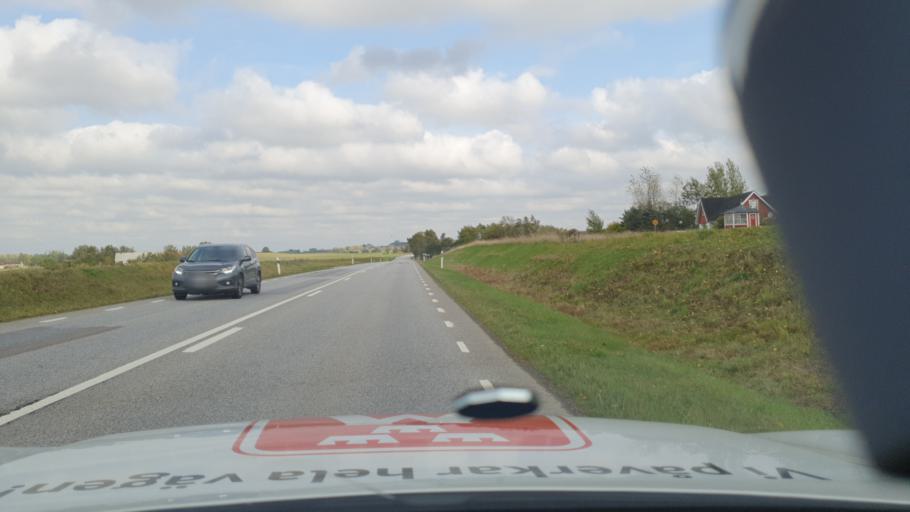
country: SE
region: Skane
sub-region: Trelleborgs Kommun
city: Trelleborg
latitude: 55.4435
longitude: 13.1823
